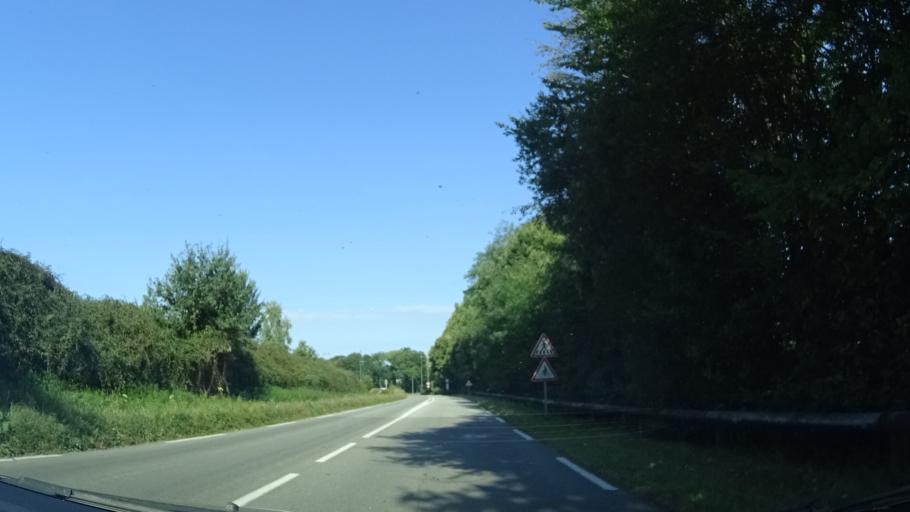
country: FR
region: Brittany
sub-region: Departement du Finistere
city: Douarnenez
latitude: 48.0848
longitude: -4.3346
